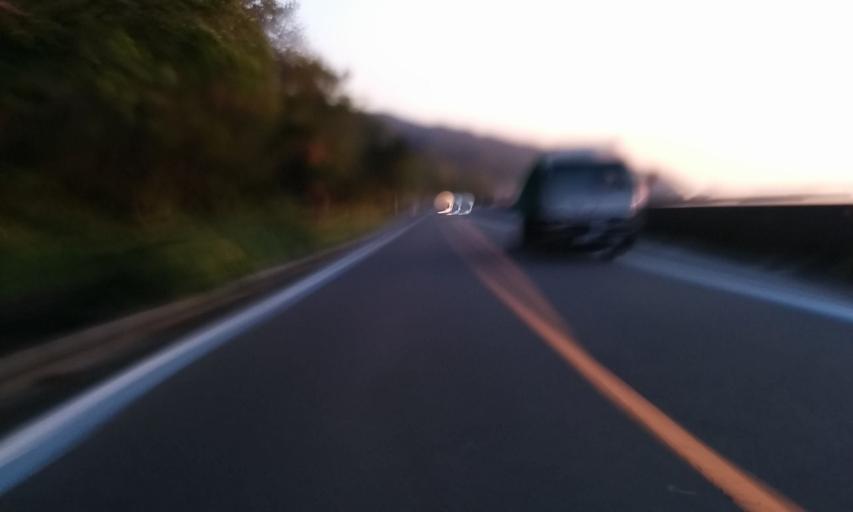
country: JP
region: Ehime
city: Iyo
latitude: 33.6563
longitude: 132.5903
